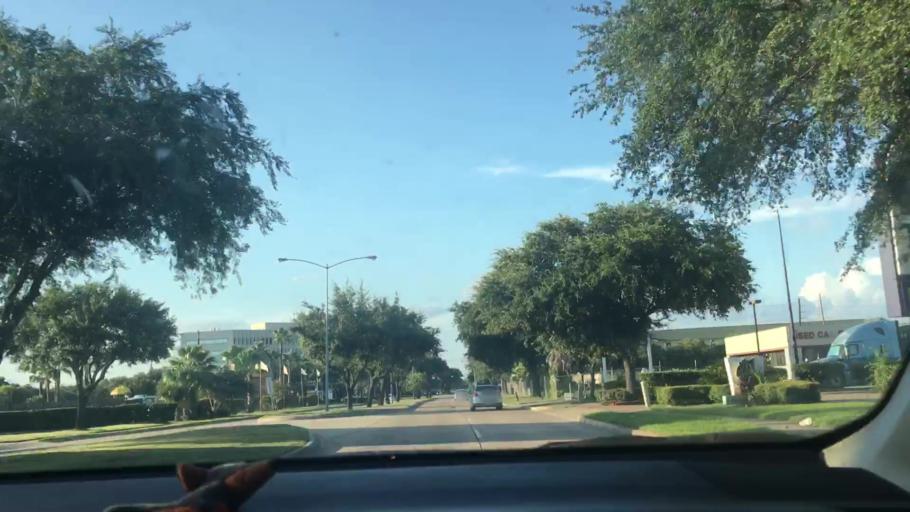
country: US
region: Texas
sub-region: Fort Bend County
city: Meadows Place
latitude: 29.6408
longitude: -95.5819
